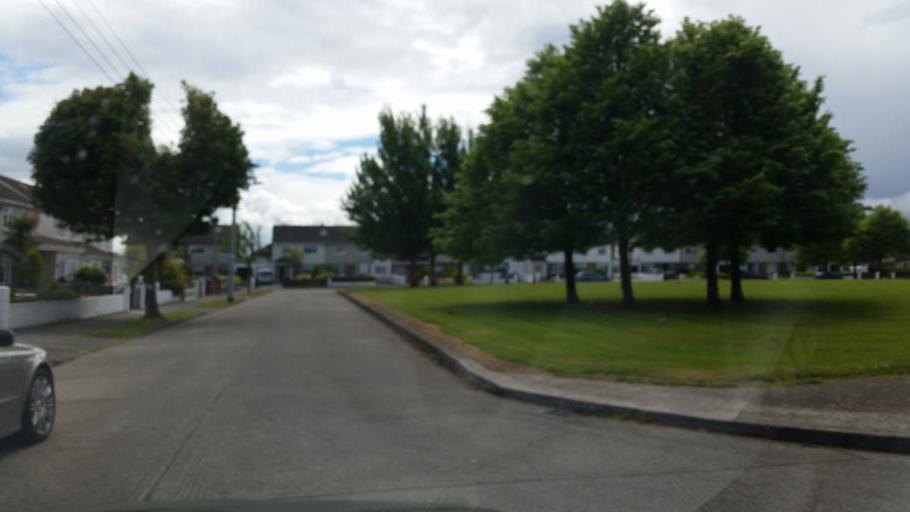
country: IE
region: Leinster
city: Ballymun
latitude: 53.3922
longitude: -6.2807
